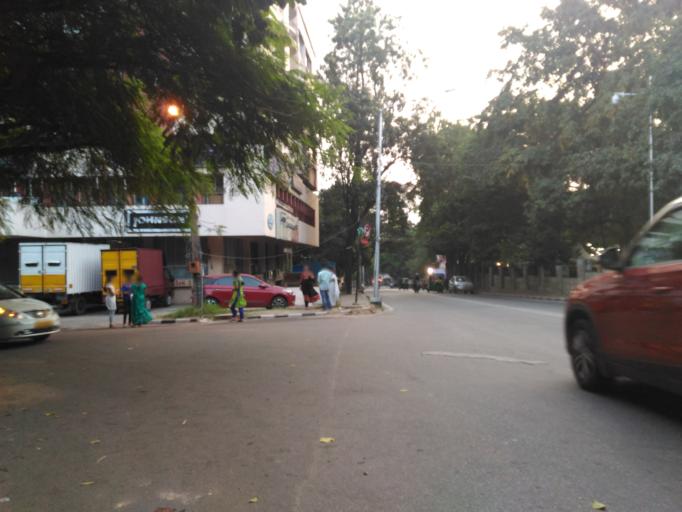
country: IN
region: Karnataka
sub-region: Bangalore Urban
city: Bangalore
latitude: 12.9896
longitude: 77.5817
